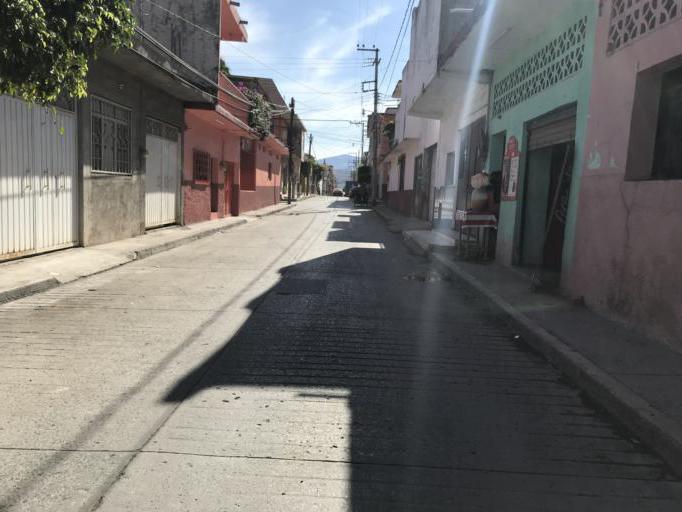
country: MX
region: Guerrero
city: Iguala de la Independencia
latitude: 18.3492
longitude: -99.5439
